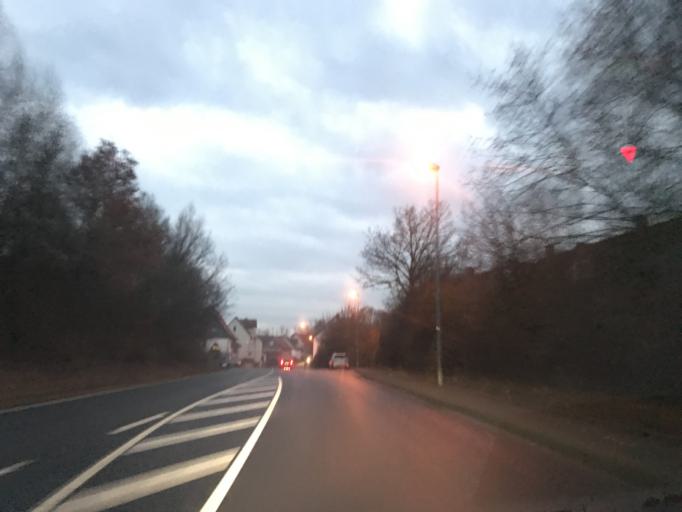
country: DE
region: Hesse
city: Trendelburg
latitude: 51.5475
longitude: 9.4147
